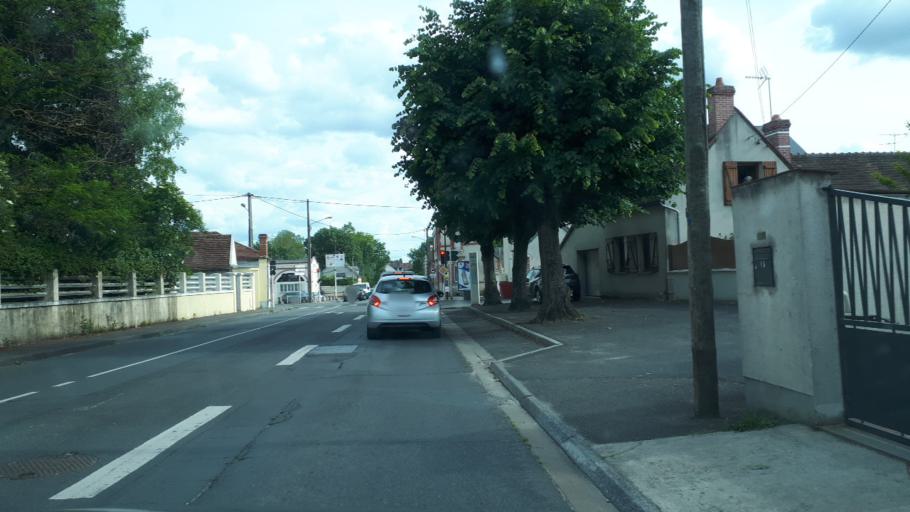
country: FR
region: Centre
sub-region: Departement du Loir-et-Cher
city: Romorantin-Lanthenay
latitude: 47.3590
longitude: 1.7394
